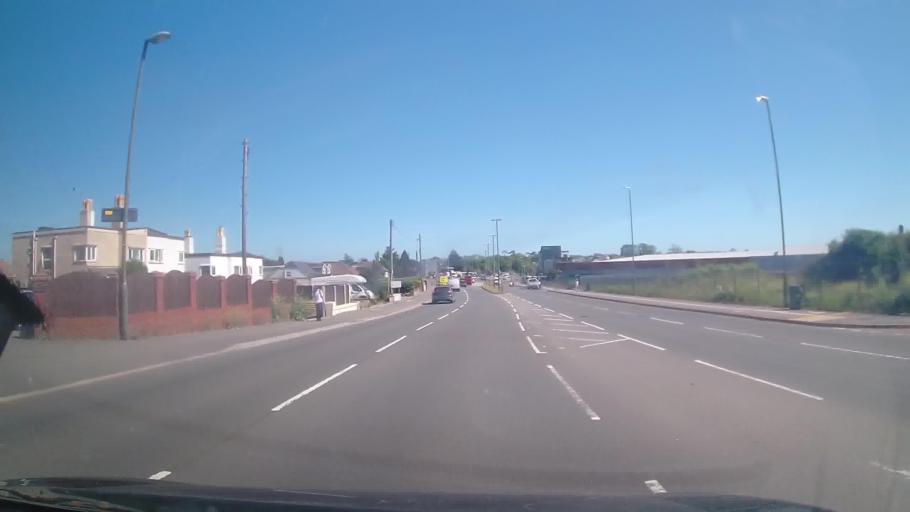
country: GB
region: England
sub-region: Borough of Torbay
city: Paignton
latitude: 50.4165
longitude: -3.5812
